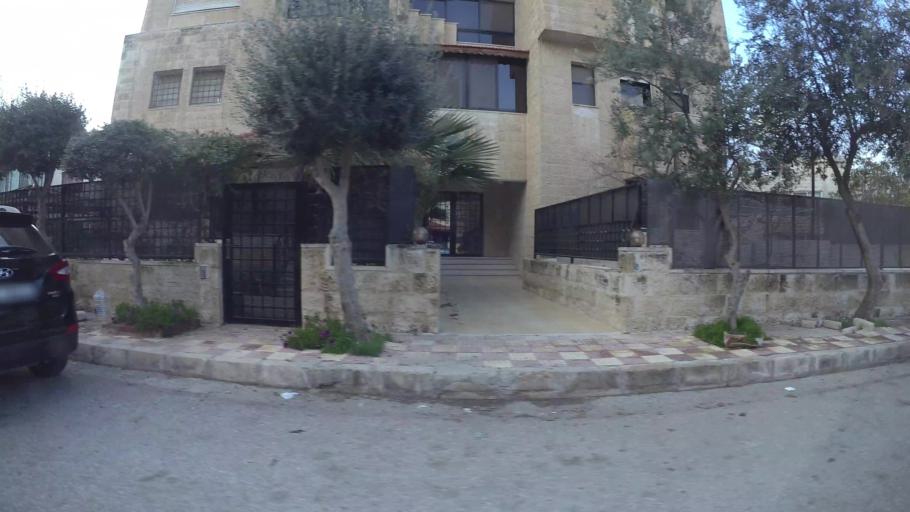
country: JO
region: Amman
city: Al Jubayhah
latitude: 31.9780
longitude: 35.8637
